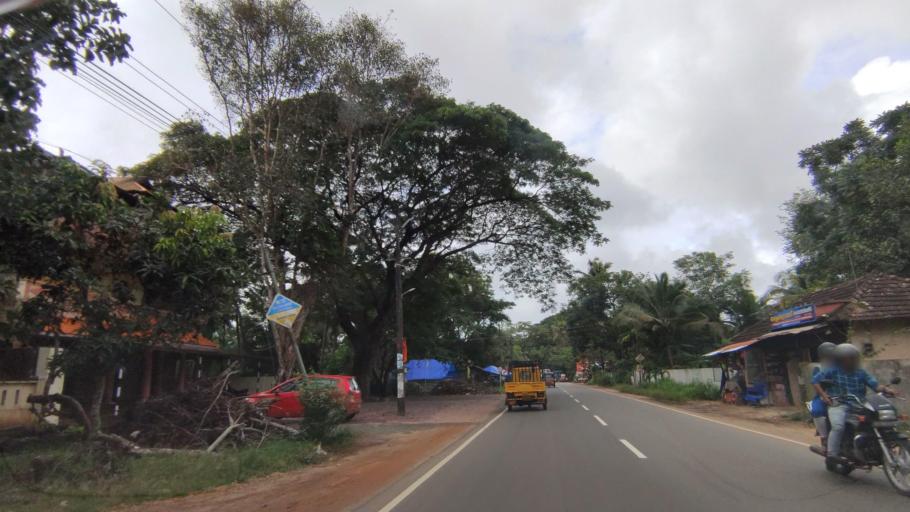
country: IN
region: Kerala
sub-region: Alappuzha
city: Shertallai
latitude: 9.6137
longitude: 76.3628
